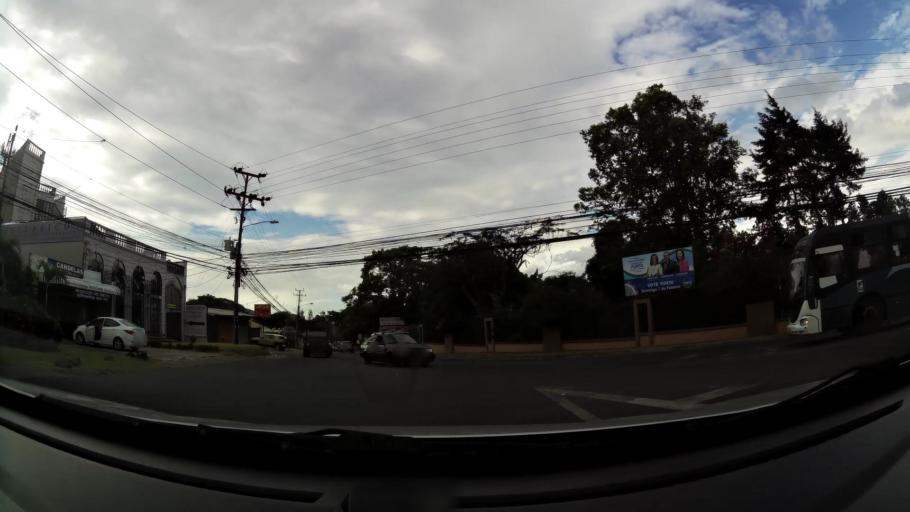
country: CR
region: San Jose
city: San Rafael
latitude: 9.9308
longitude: -84.1508
